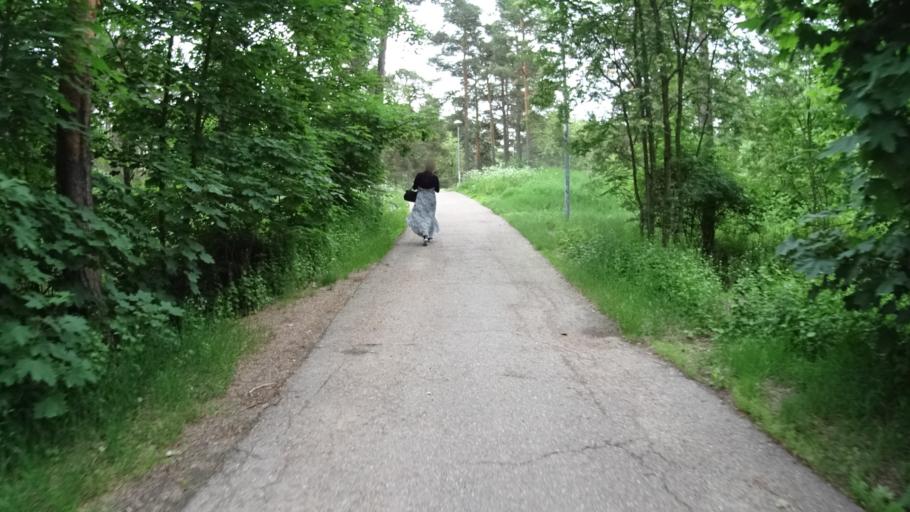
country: FI
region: Uusimaa
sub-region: Helsinki
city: Kilo
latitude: 60.2793
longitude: 24.8453
